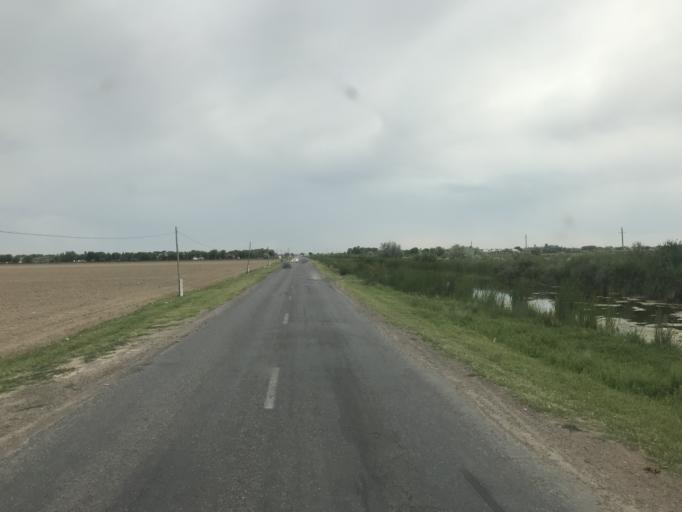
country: KZ
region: Ongtustik Qazaqstan
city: Asykata
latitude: 40.9197
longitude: 68.3991
